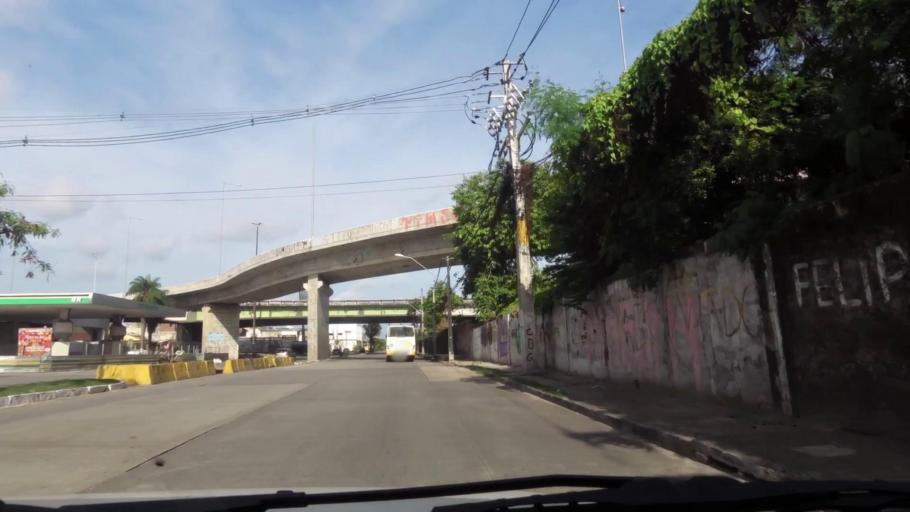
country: BR
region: Pernambuco
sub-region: Recife
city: Recife
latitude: -8.0753
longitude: -34.8902
